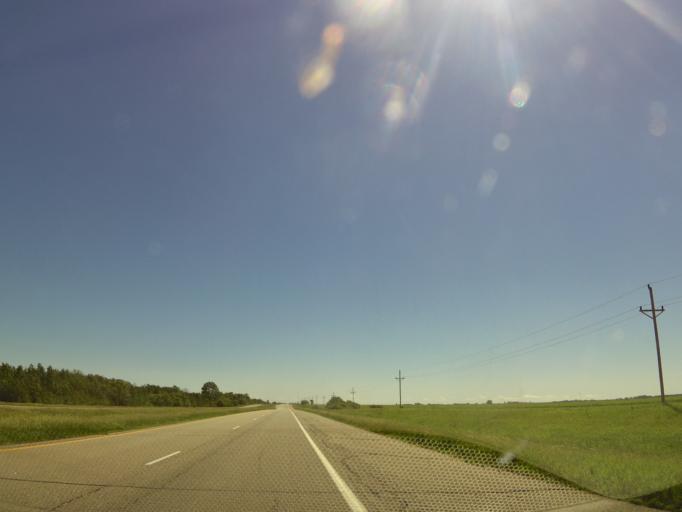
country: US
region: Minnesota
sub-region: Red Lake County
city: Red Lake Falls
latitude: 47.7602
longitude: -96.3170
